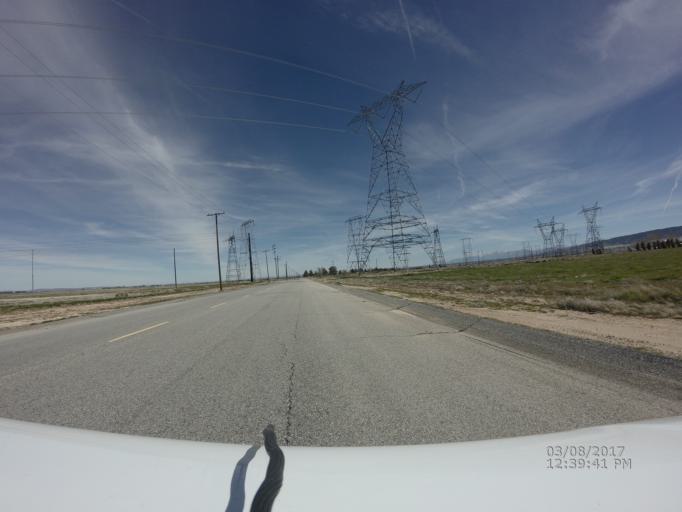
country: US
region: California
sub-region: Los Angeles County
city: Leona Valley
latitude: 34.7038
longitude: -118.3173
